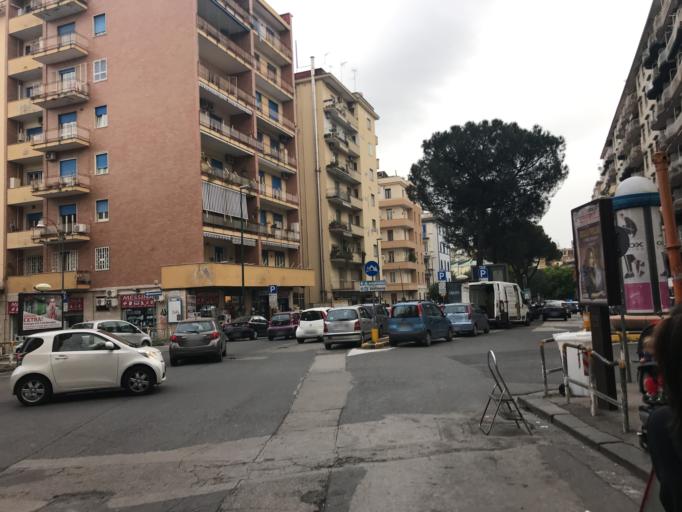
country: IT
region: Campania
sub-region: Provincia di Napoli
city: Napoli
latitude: 40.8510
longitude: 14.2273
